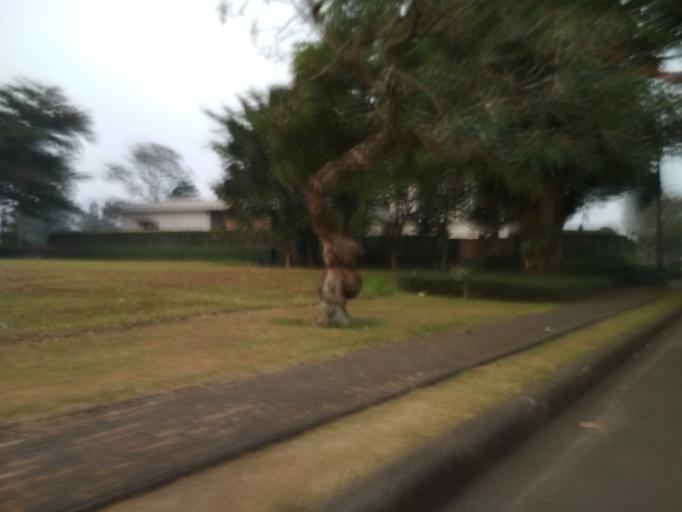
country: ID
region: West Java
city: Caringin
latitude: -6.6639
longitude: 106.8298
